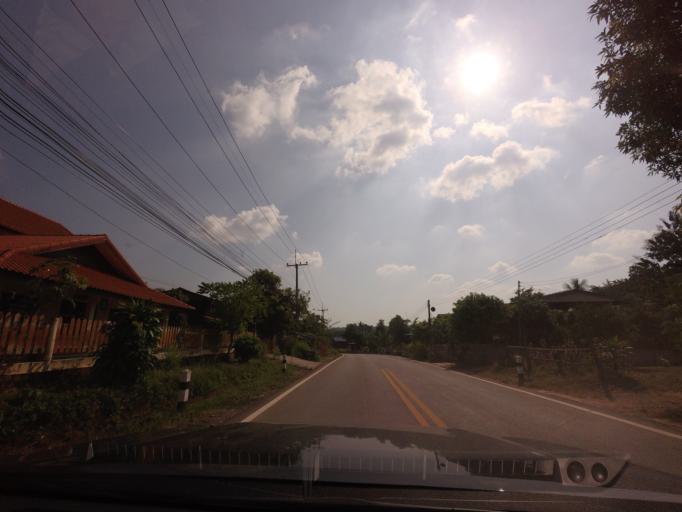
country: TH
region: Nan
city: Santi Suk
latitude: 18.9580
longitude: 100.9239
